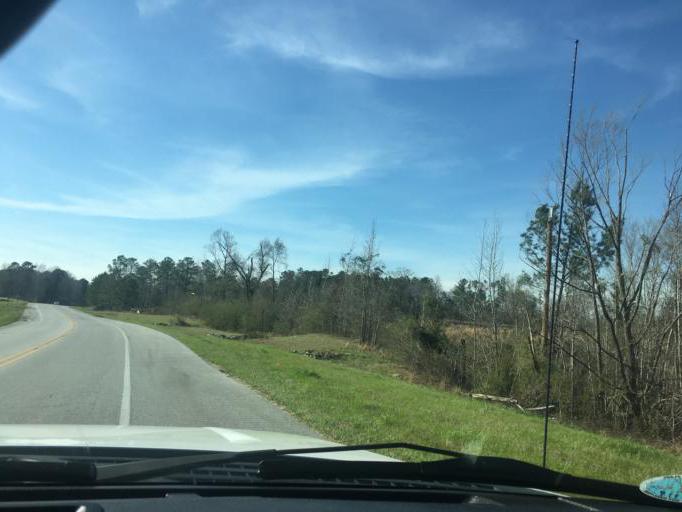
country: US
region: Alabama
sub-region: Lee County
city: Auburn
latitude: 32.4325
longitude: -85.4681
